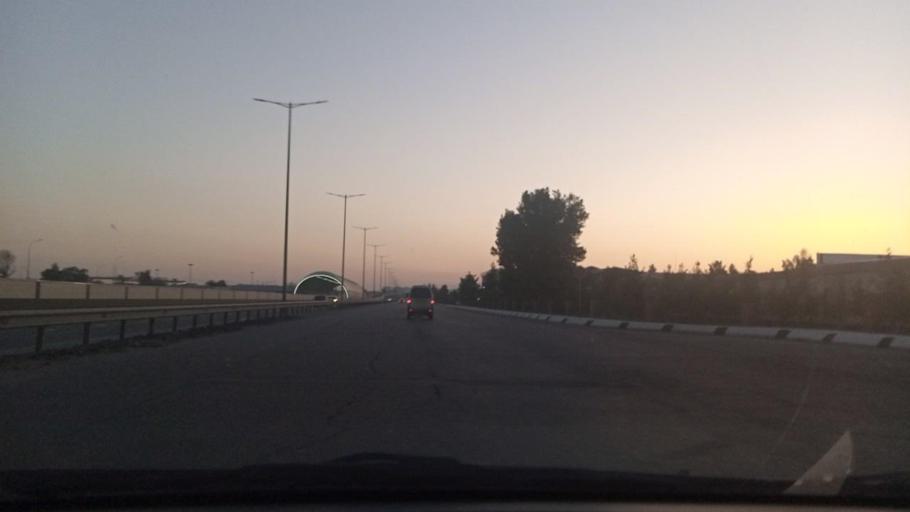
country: UZ
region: Toshkent Shahri
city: Bektemir
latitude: 41.2537
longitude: 69.3573
